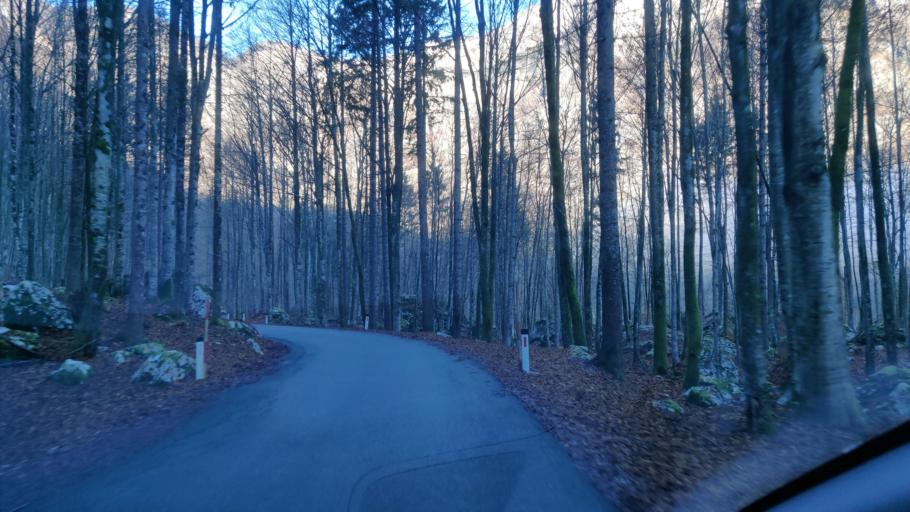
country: SI
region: Tolmin
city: Tolmin
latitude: 46.2776
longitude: 13.8128
